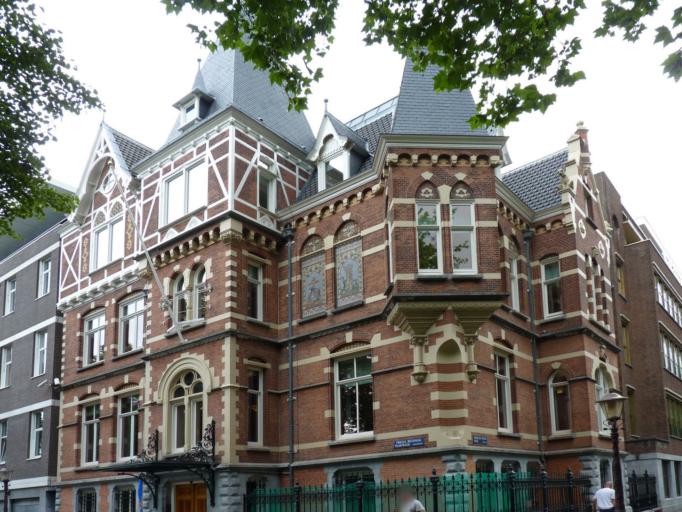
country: NL
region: North Holland
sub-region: Gemeente Amsterdam
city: Amsterdam
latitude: 52.3585
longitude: 4.8929
